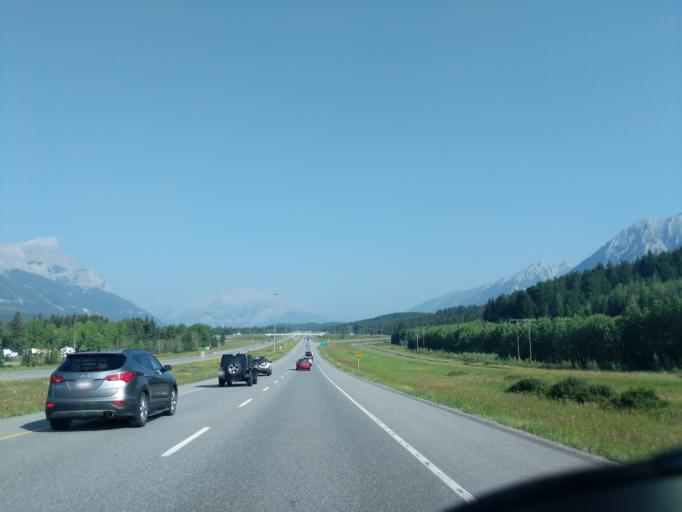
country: CA
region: Alberta
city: Canmore
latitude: 51.1046
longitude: -115.3618
